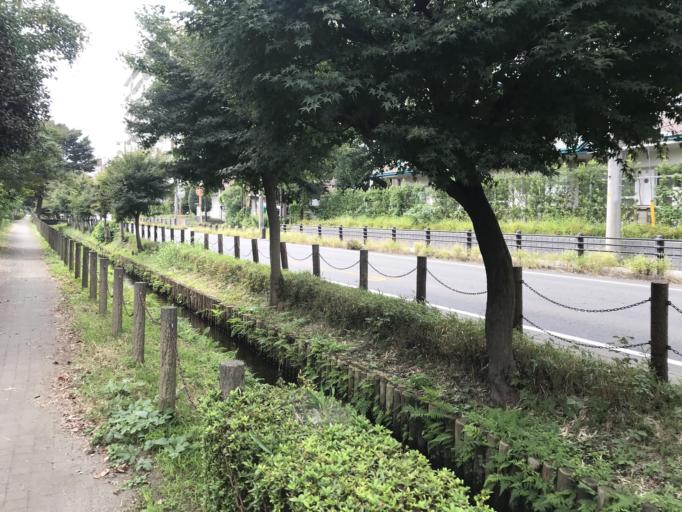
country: JP
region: Tokyo
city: Tanashicho
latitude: 35.7676
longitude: 139.5209
